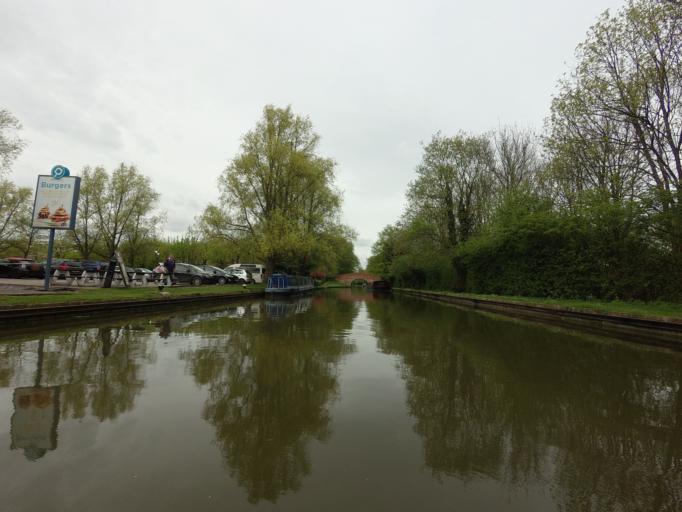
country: GB
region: England
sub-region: Milton Keynes
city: Milton Keynes
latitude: 52.0282
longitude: -0.7307
